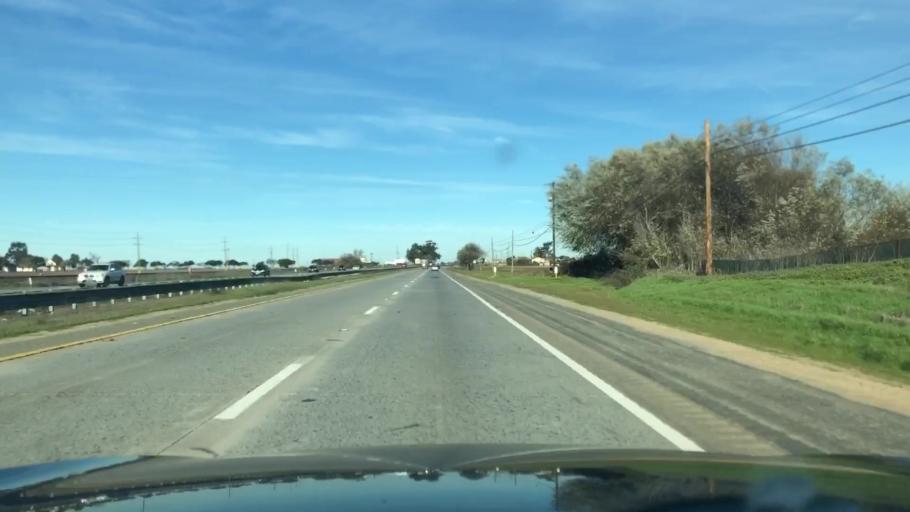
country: US
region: California
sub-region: Monterey County
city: Chualar
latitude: 36.5616
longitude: -121.5098
